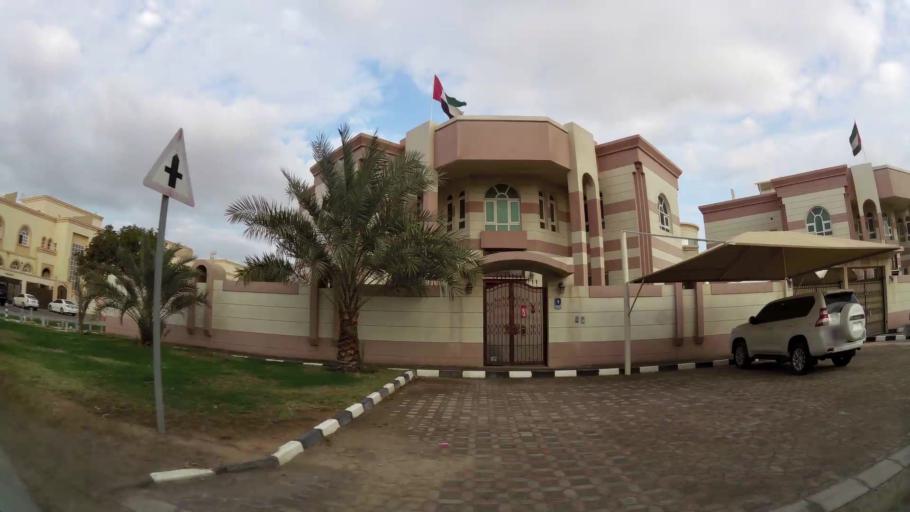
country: AE
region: Abu Dhabi
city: Abu Dhabi
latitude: 24.3593
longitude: 54.5526
